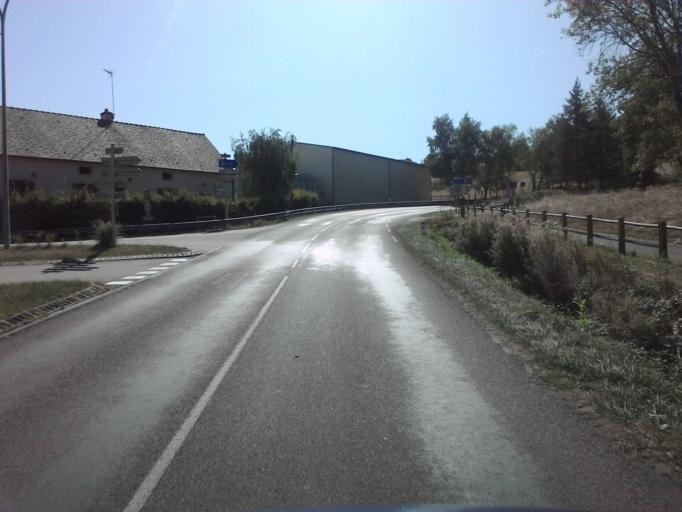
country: FR
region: Bourgogne
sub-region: Departement de la Cote-d'Or
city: Semur-en-Auxois
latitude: 47.4708
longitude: 4.3553
